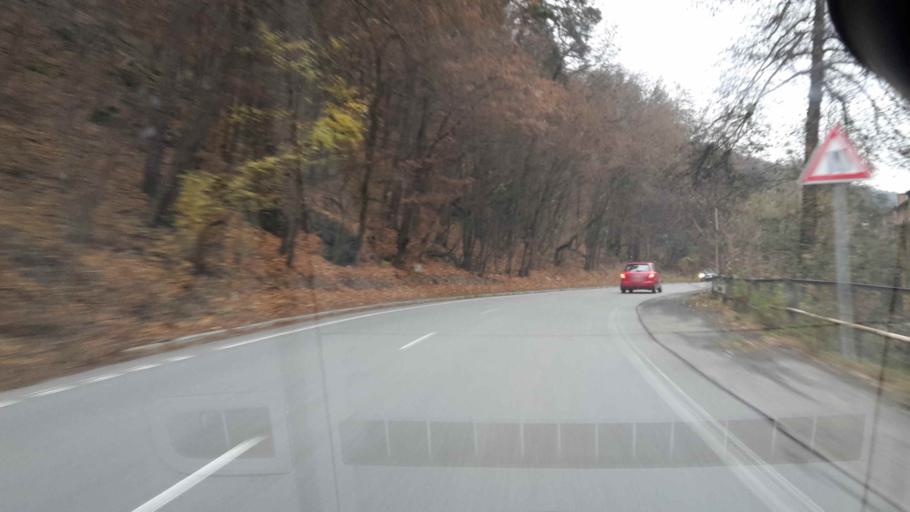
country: CZ
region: South Moravian
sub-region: Okres Blansko
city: Blansko
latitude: 49.3533
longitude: 16.6698
